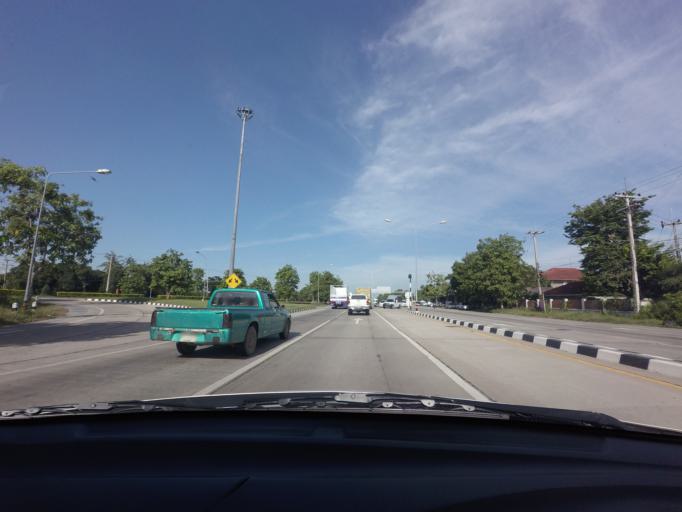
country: TH
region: Suphan Buri
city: Suphan Buri
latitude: 14.4483
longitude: 100.1111
